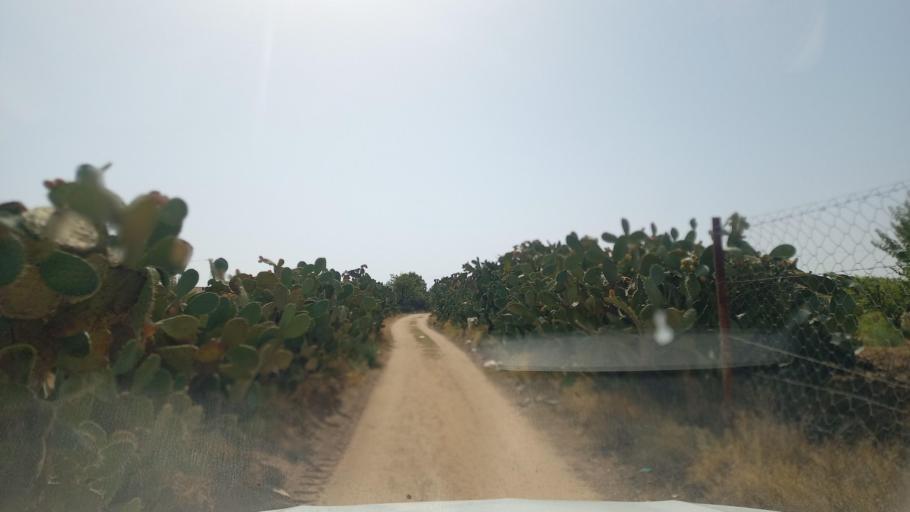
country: TN
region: Al Qasrayn
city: Kasserine
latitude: 35.2385
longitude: 9.0516
